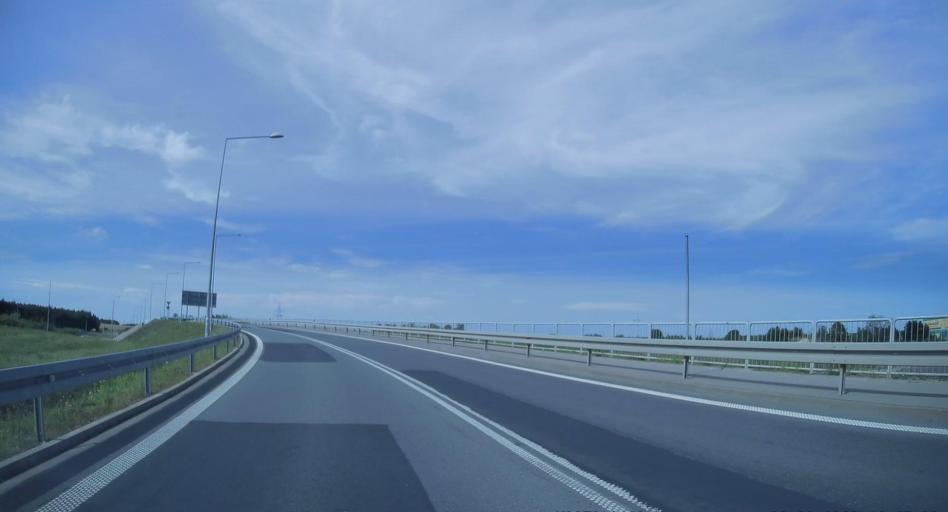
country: PL
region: Lodz Voivodeship
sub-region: Powiat tomaszowski
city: Tomaszow Mazowiecki
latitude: 51.5485
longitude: 19.9900
